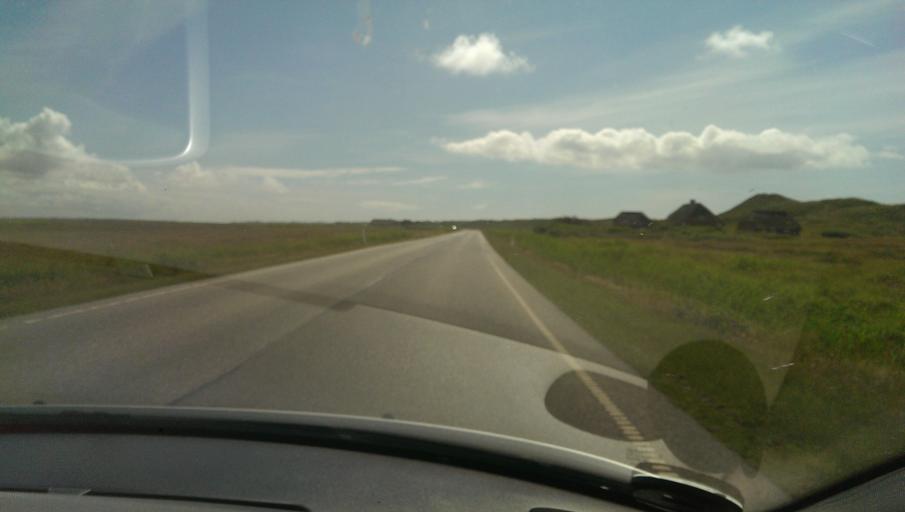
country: DK
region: Central Jutland
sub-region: Ringkobing-Skjern Kommune
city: Ringkobing
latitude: 56.2158
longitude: 8.1378
